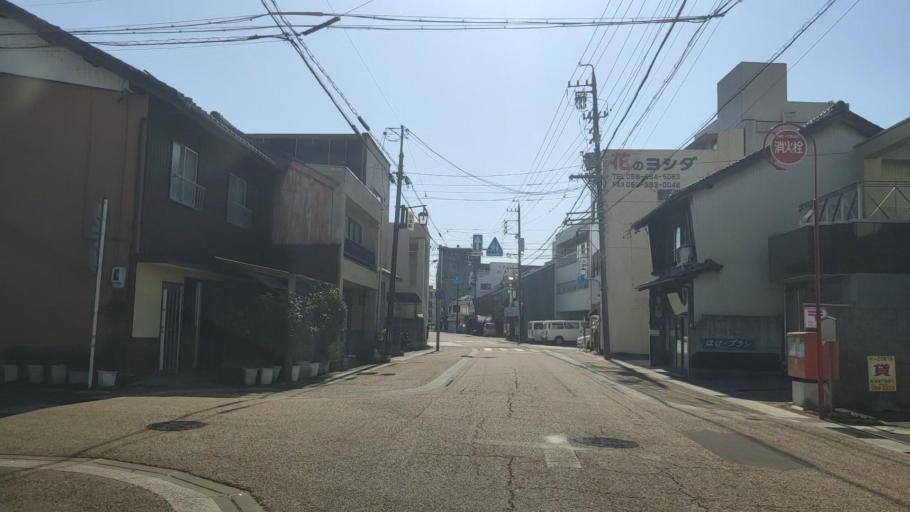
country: JP
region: Gifu
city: Gifu-shi
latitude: 35.4277
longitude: 136.7649
